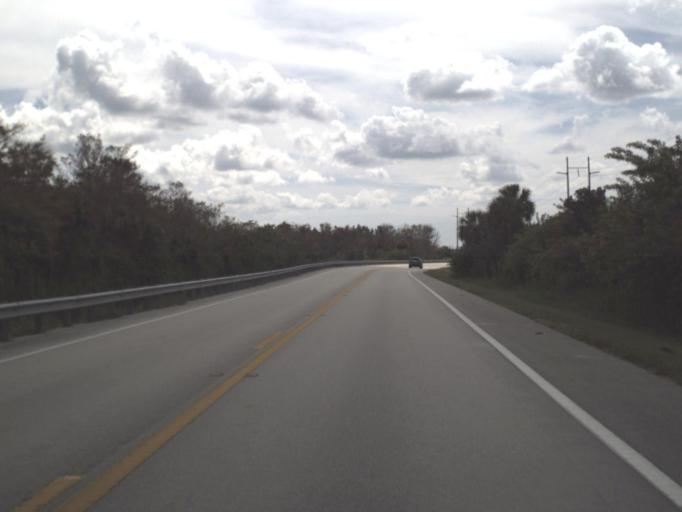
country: US
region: Florida
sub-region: Collier County
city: Marco
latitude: 25.9229
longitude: -81.3581
